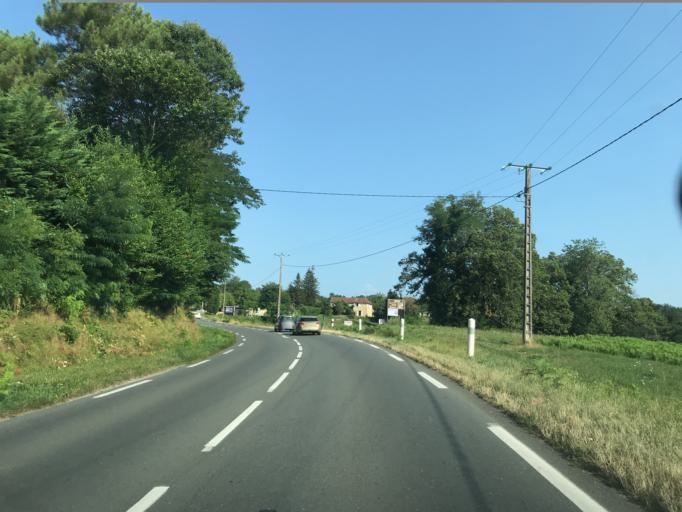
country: FR
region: Aquitaine
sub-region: Departement de la Dordogne
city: Sarlat-la-Caneda
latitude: 44.9264
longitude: 1.2072
